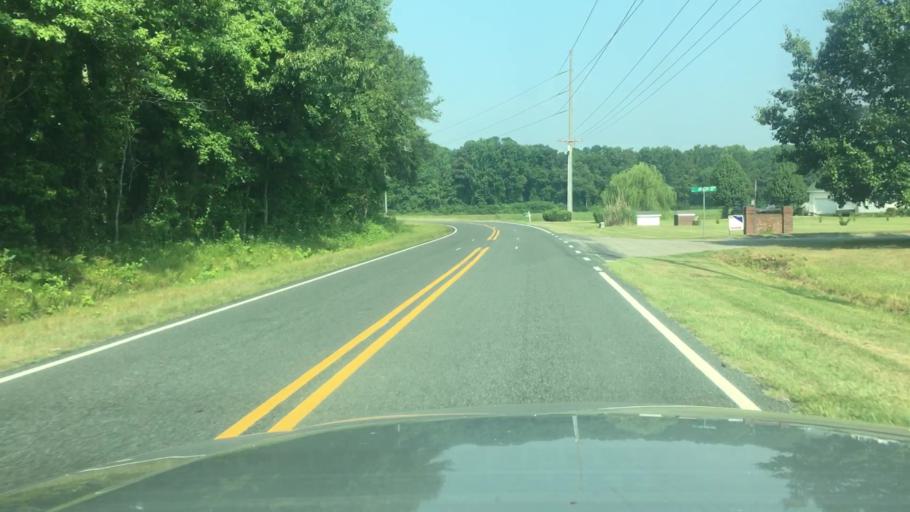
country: US
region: North Carolina
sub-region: Cumberland County
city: Hope Mills
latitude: 34.8981
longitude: -78.8925
